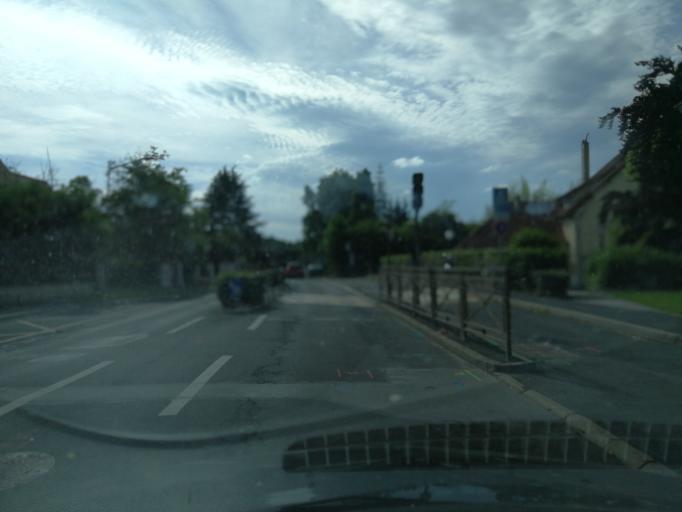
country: FR
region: Ile-de-France
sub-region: Departement des Yvelines
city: Saint-Remy-les-Chevreuse
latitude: 48.6980
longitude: 2.1040
